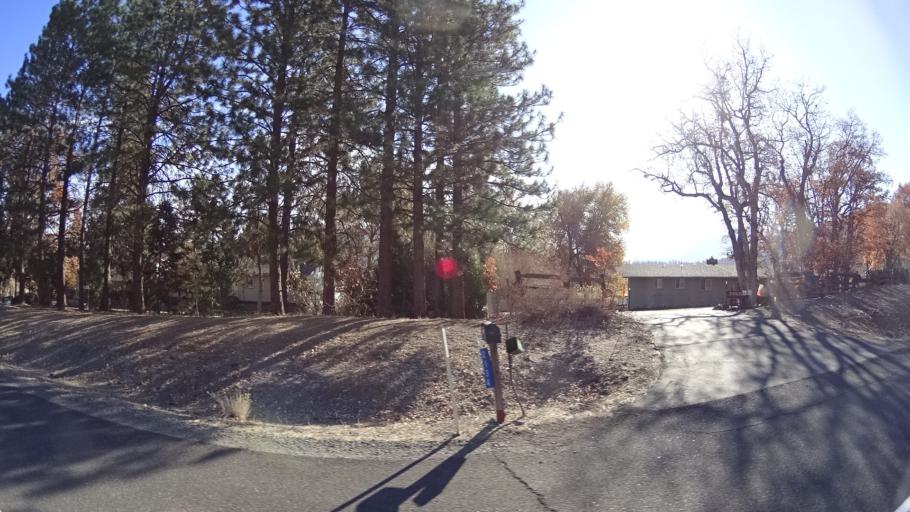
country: US
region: California
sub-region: Siskiyou County
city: Yreka
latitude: 41.6946
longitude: -122.6503
